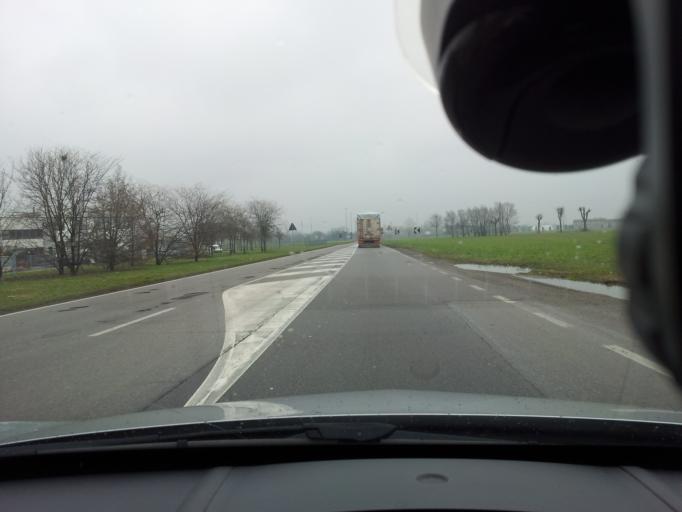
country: IT
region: Lombardy
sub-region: Provincia di Bergamo
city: Cavernago
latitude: 45.6174
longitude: 9.7791
